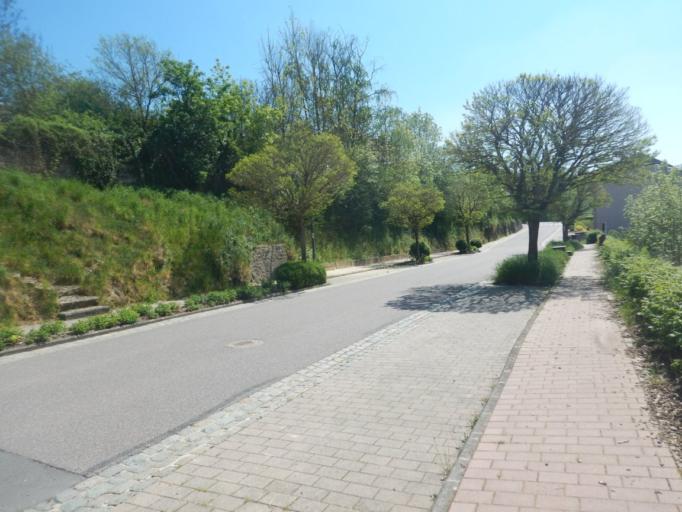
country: LU
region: Diekirch
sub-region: Canton de Diekirch
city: Bourscheid
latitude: 49.8988
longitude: 6.0901
